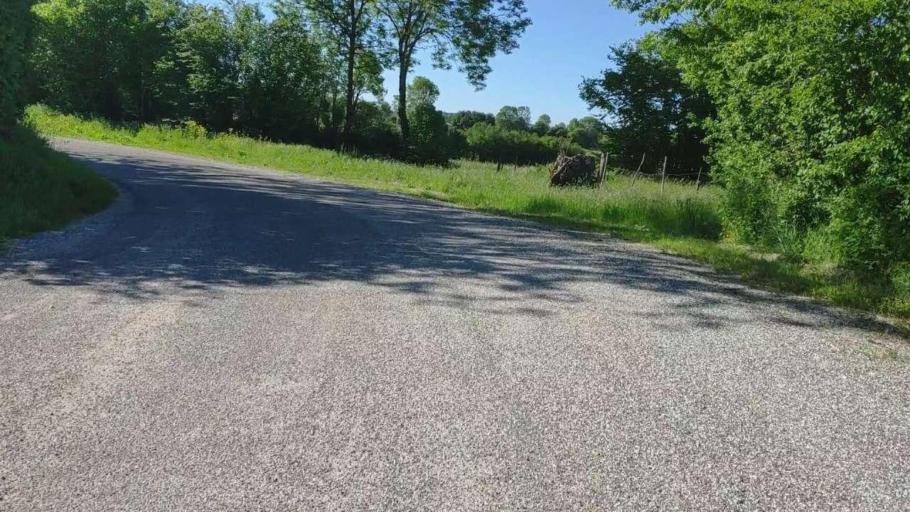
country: FR
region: Franche-Comte
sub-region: Departement du Jura
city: Perrigny
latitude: 46.6867
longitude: 5.6483
